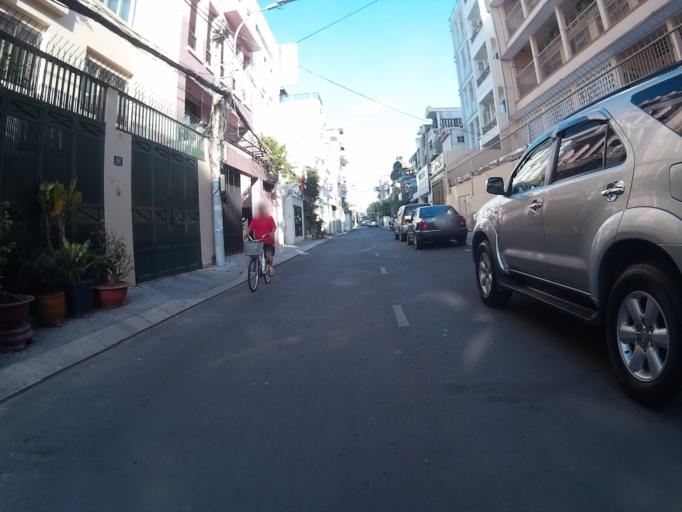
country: VN
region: Ho Chi Minh City
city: Quan Phu Nhuan
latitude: 10.7932
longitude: 106.6875
